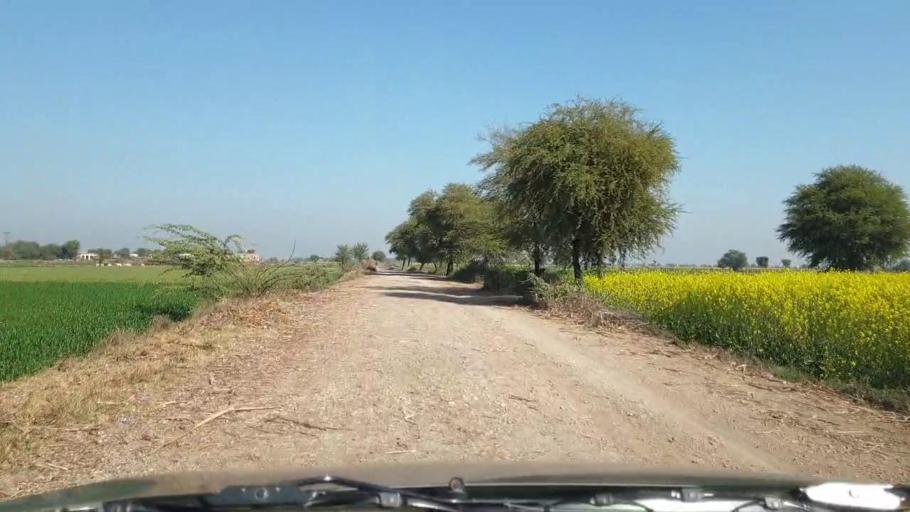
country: PK
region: Sindh
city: Jhol
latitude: 25.9611
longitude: 68.8230
